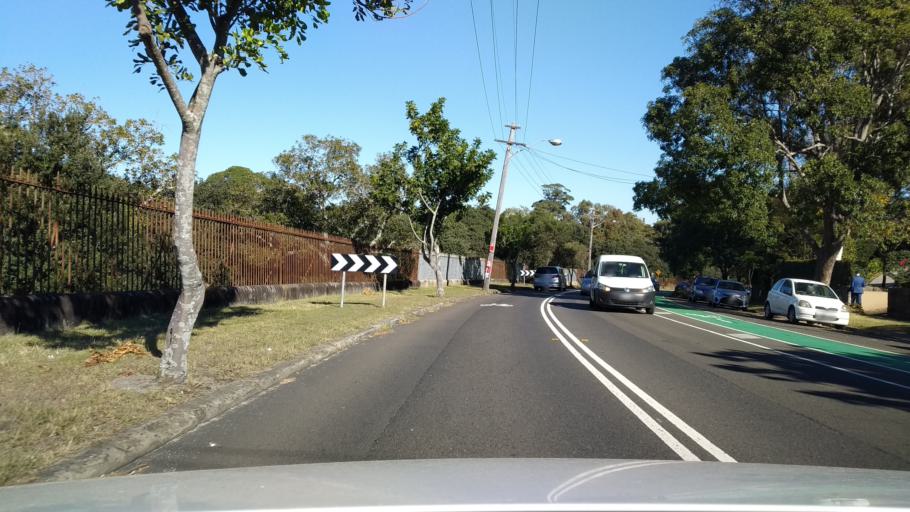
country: AU
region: New South Wales
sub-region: Woollahra
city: Woollahra
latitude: -33.8966
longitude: 151.2293
